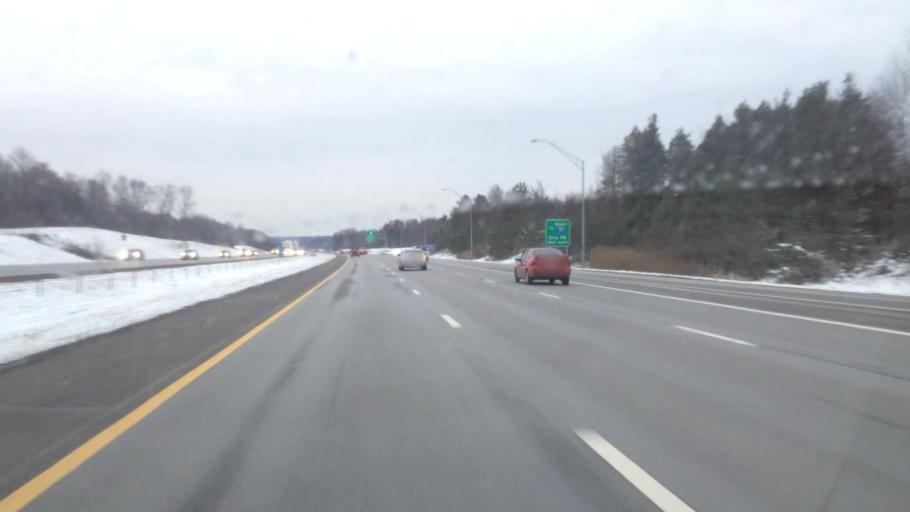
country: US
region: Ohio
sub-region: Medina County
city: Brunswick
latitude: 41.2074
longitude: -81.7936
